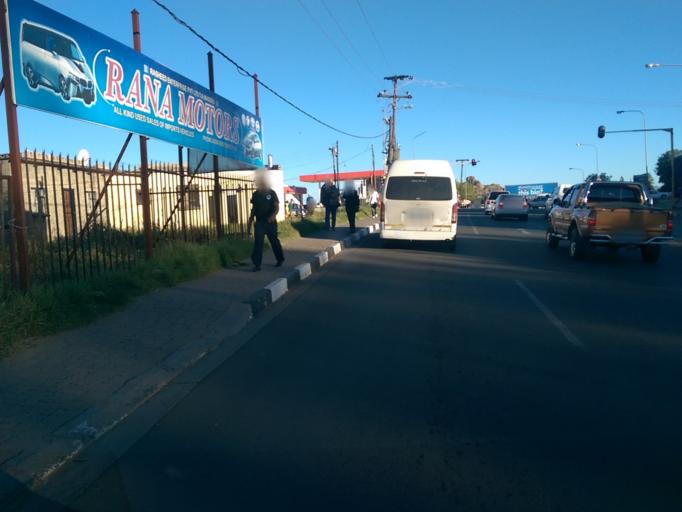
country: LS
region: Maseru
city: Maseru
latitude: -29.3335
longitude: 27.5083
